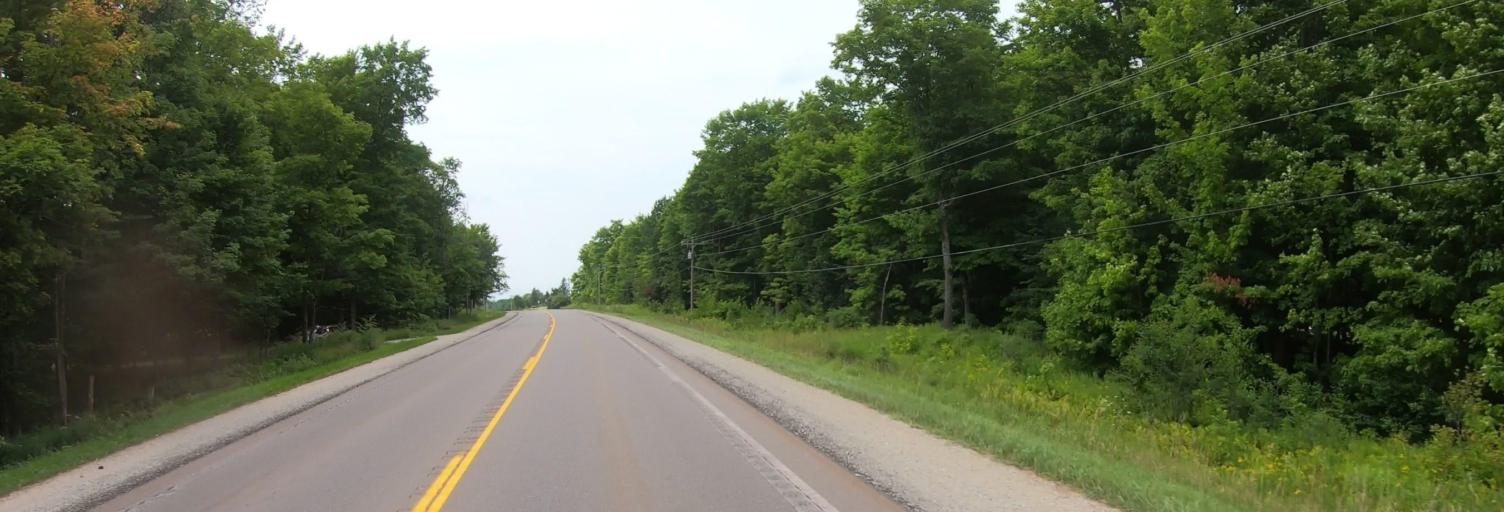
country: US
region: Michigan
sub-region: Alger County
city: Munising
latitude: 46.3548
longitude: -86.9940
